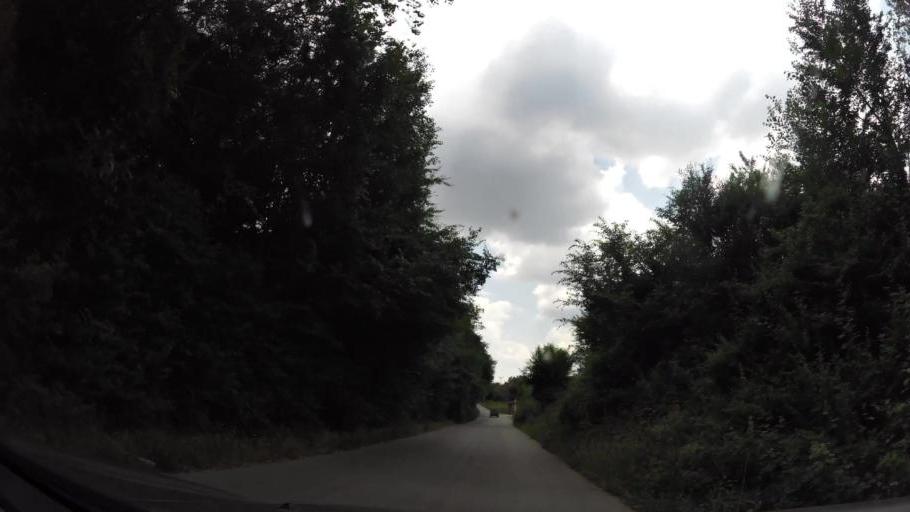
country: GR
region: West Macedonia
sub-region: Nomos Kozanis
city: Kozani
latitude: 40.2985
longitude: 21.8042
